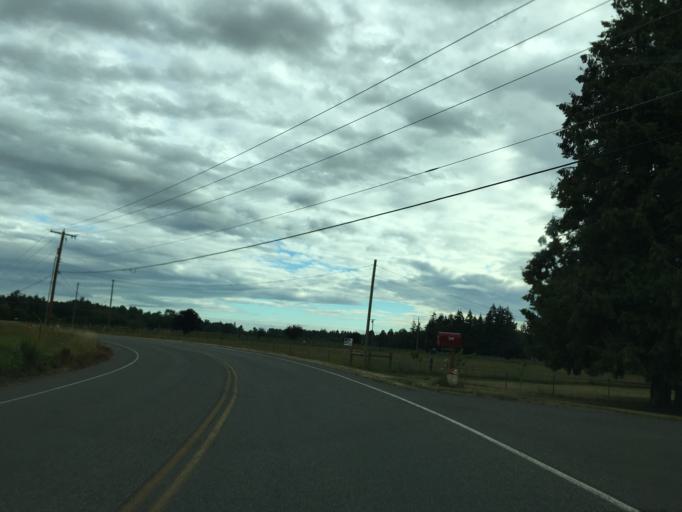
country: US
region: Washington
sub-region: Whatcom County
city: Lynden
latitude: 48.8911
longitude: -122.5076
